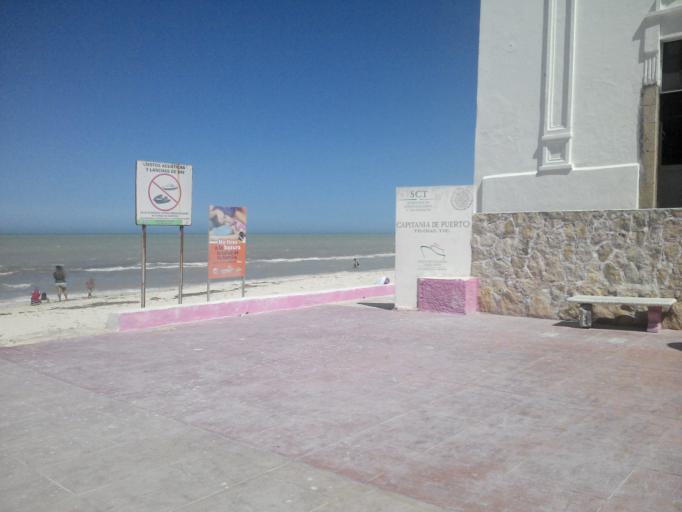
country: MX
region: Yucatan
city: Telchac Puerto
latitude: 21.3439
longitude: -89.2638
